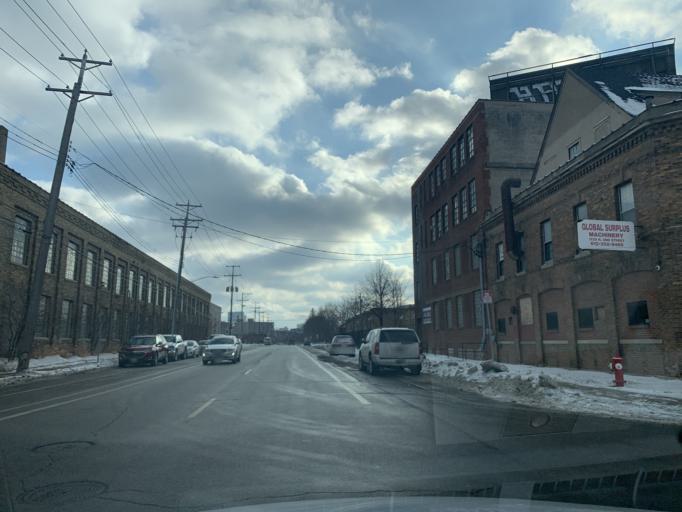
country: US
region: Minnesota
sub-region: Hennepin County
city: Minneapolis
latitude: 44.9975
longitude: -93.2799
